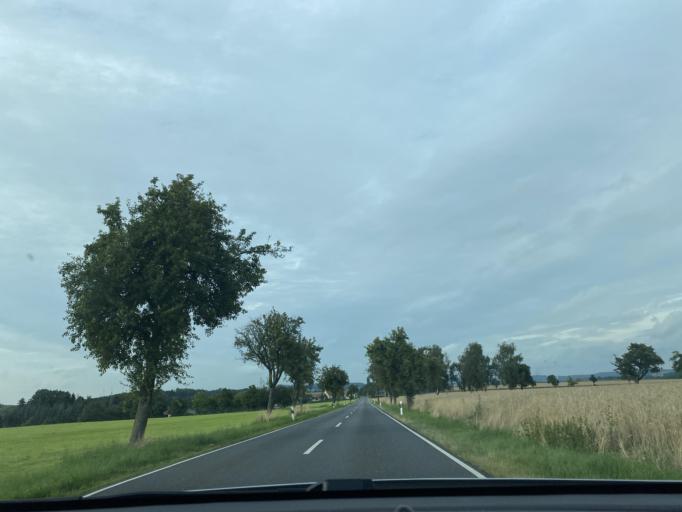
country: DE
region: Saxony
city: Bernstadt
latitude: 51.0202
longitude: 14.8030
